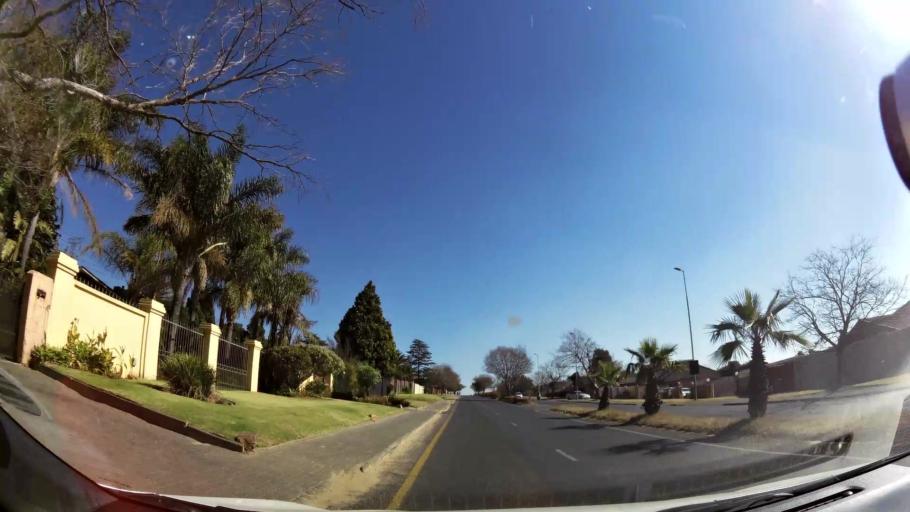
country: ZA
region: Gauteng
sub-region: City of Johannesburg Metropolitan Municipality
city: Johannesburg
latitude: -26.2725
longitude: 27.9937
